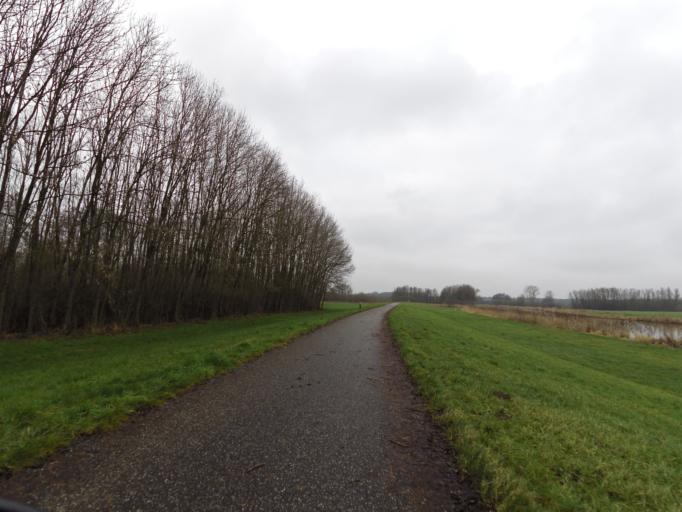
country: NL
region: Gelderland
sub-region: Gemeente Doetinchem
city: Doetinchem
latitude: 51.9826
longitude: 6.2354
